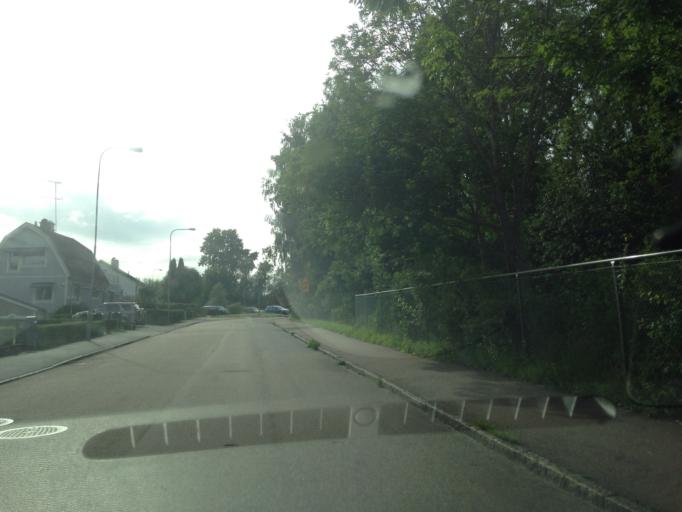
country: SE
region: Vaestra Goetaland
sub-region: Goteborg
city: Goeteborg
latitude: 57.7530
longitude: 11.9712
